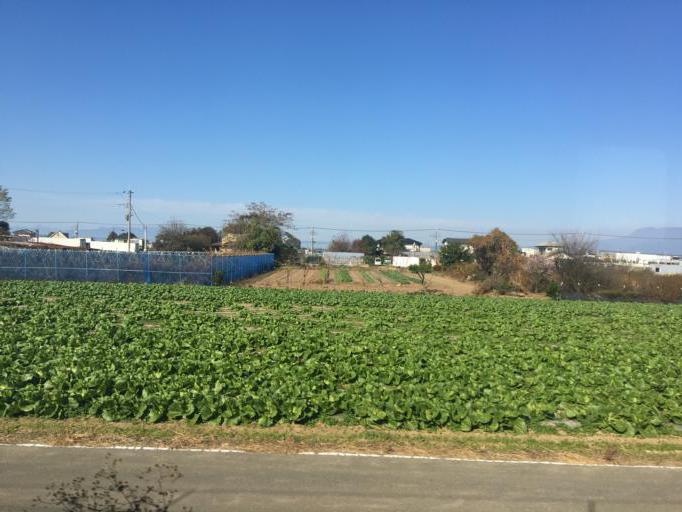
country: JP
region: Gunma
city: Isesaki
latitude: 36.3431
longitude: 139.2240
